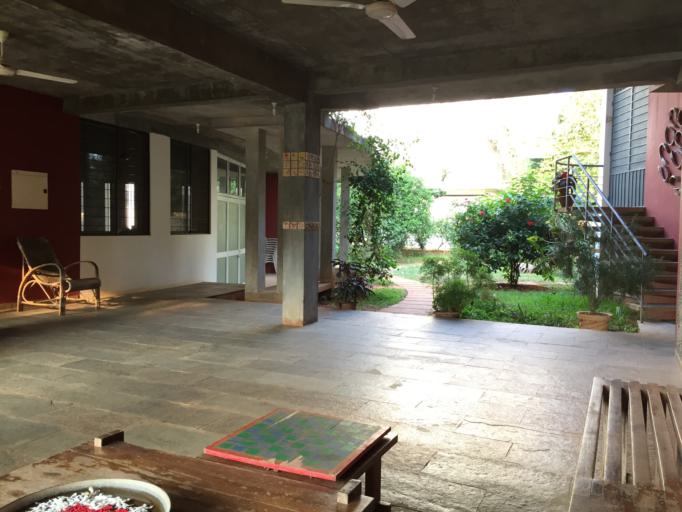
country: IN
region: Tamil Nadu
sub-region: Villupuram
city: Auroville
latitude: 12.0106
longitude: 79.8117
